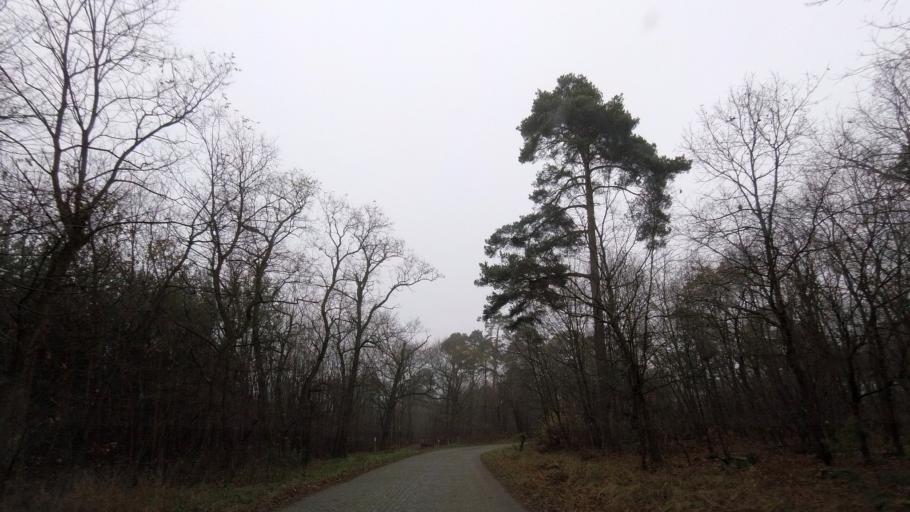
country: DE
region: Brandenburg
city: Treuenbrietzen
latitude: 52.0534
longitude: 12.8975
